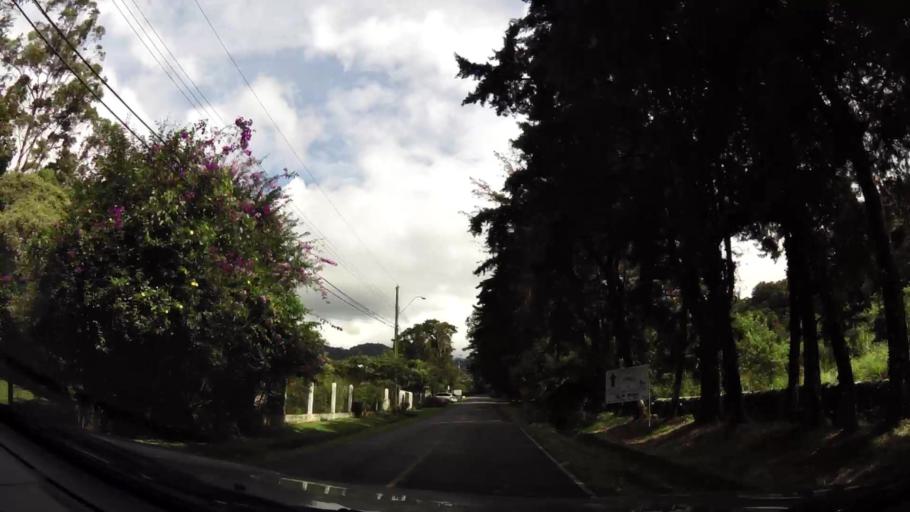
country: PA
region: Chiriqui
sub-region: Distrito Boquete
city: Boquete
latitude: 8.7967
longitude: -82.4289
